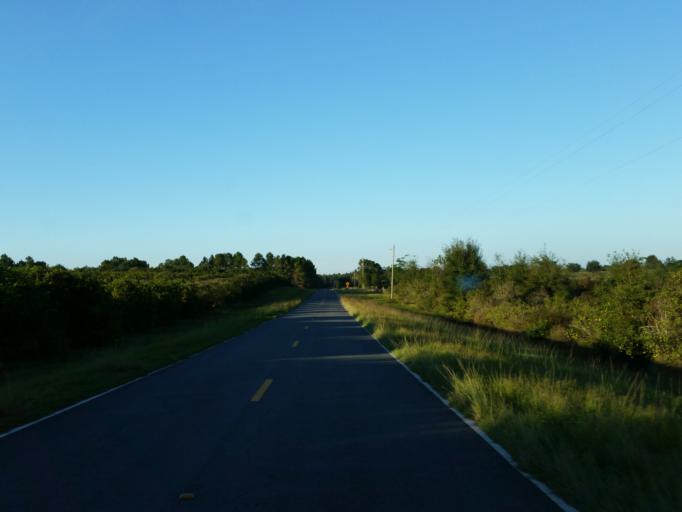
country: US
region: Florida
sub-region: Hernando County
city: Hill 'n Dale
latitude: 28.4462
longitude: -82.2698
